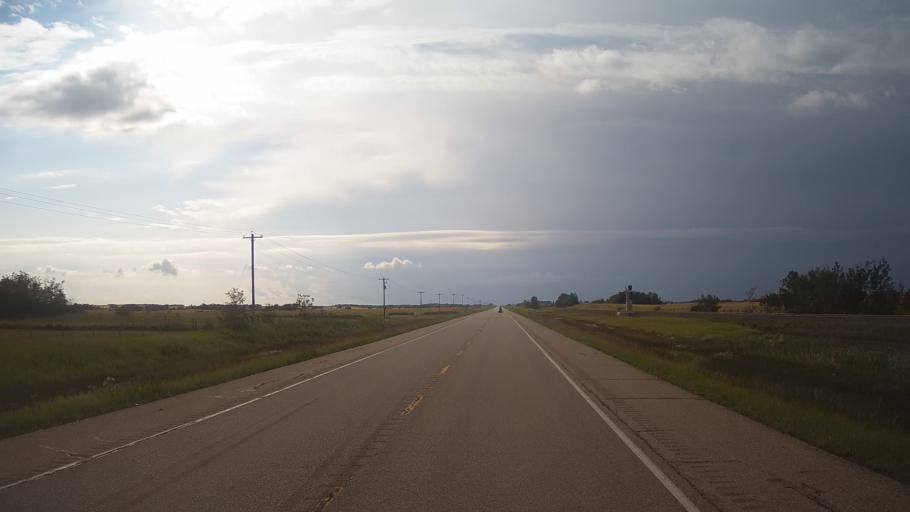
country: CA
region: Alberta
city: Viking
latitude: 53.1489
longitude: -111.9653
